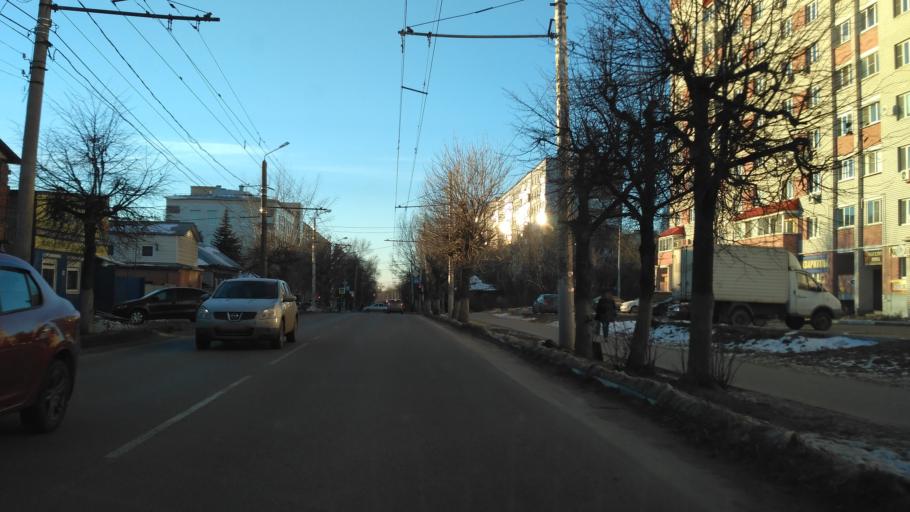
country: RU
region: Tula
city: Tula
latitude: 54.2074
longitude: 37.6103
